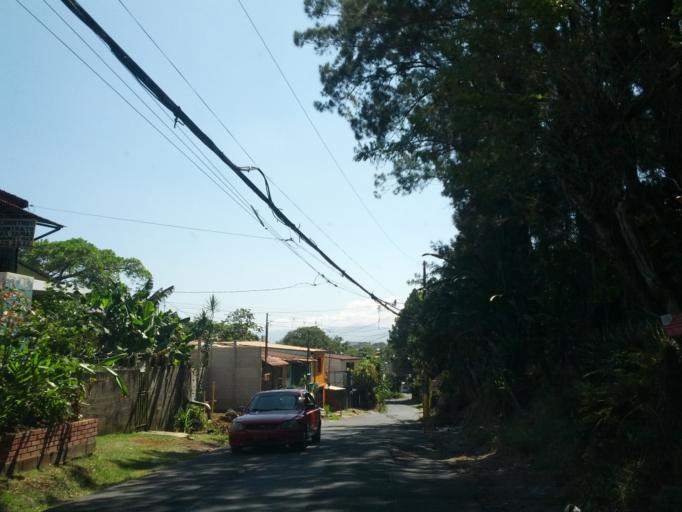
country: CR
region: Alajuela
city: Alajuela
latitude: 10.0080
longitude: -84.1885
